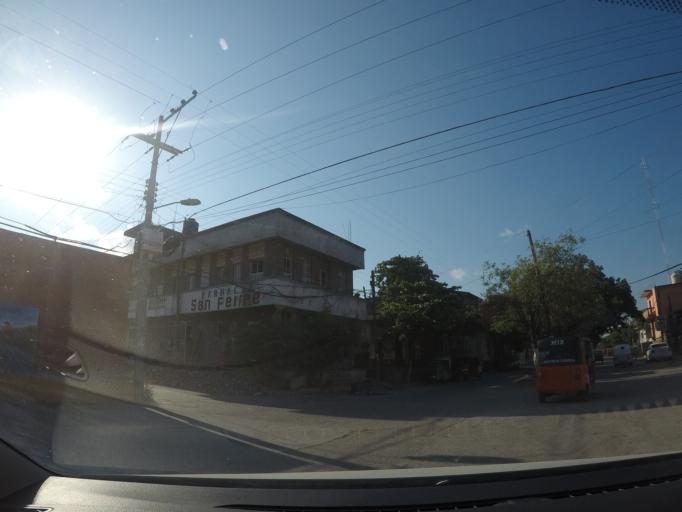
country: MX
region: Oaxaca
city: Juchitan de Zaragoza
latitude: 16.4215
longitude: -95.0233
